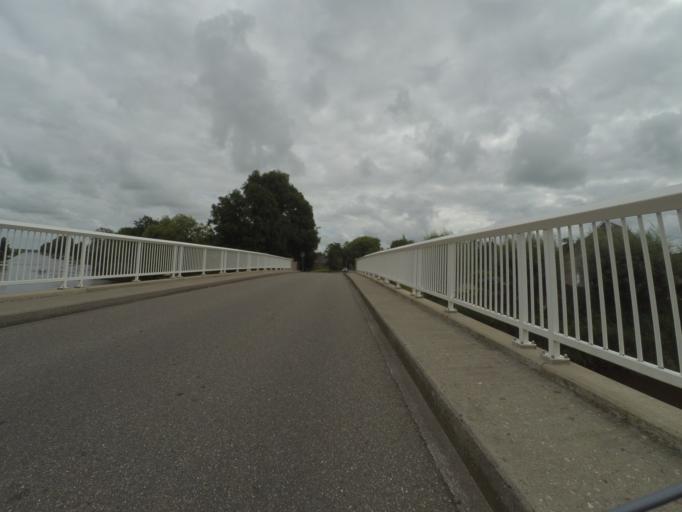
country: NL
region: Friesland
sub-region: Gemeente Kollumerland en Nieuwkruisland
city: Kollumerzwaag
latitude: 53.2945
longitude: 6.0851
